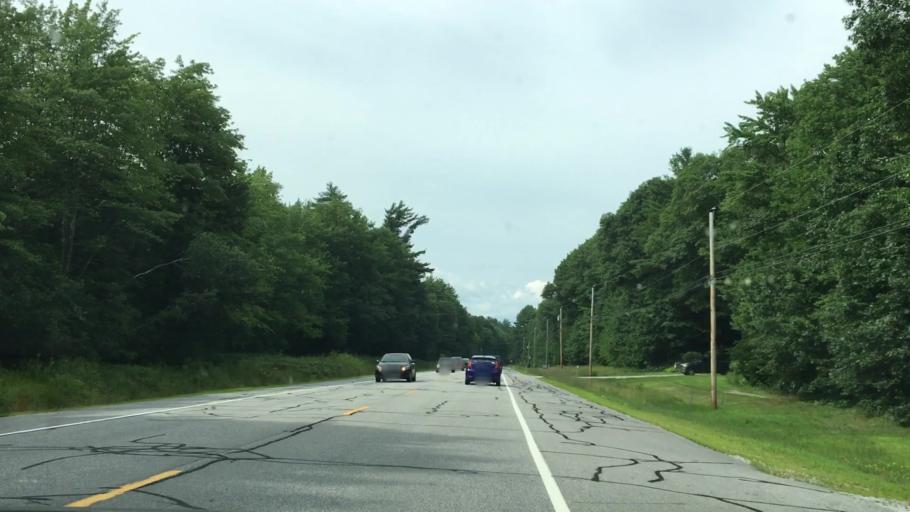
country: US
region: New Hampshire
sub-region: Hillsborough County
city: Hillsborough
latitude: 43.0873
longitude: -71.9187
